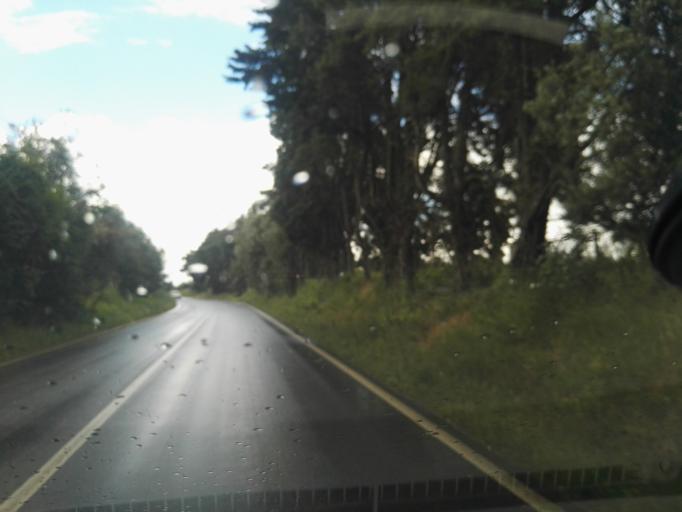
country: PT
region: Santarem
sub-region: Golega
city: Golega
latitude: 39.4215
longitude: -8.4965
